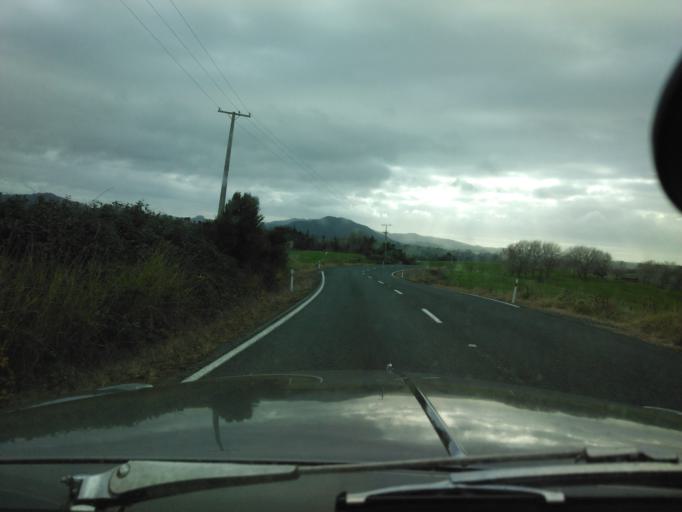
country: NZ
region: Auckland
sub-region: Auckland
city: Wellsford
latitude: -36.1761
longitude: 174.4154
